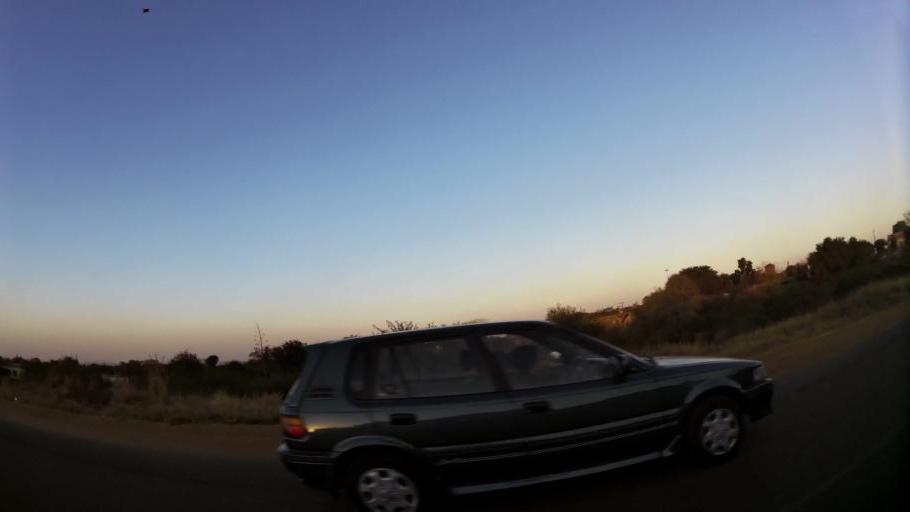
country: ZA
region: North-West
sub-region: Bojanala Platinum District Municipality
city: Rustenburg
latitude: -25.6189
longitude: 27.1952
